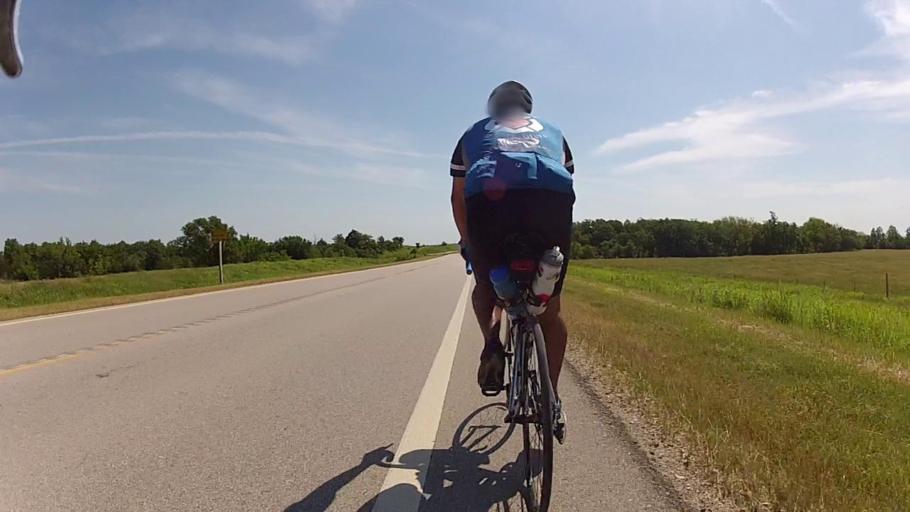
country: US
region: Kansas
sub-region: Chautauqua County
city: Sedan
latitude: 37.1087
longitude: -96.5334
